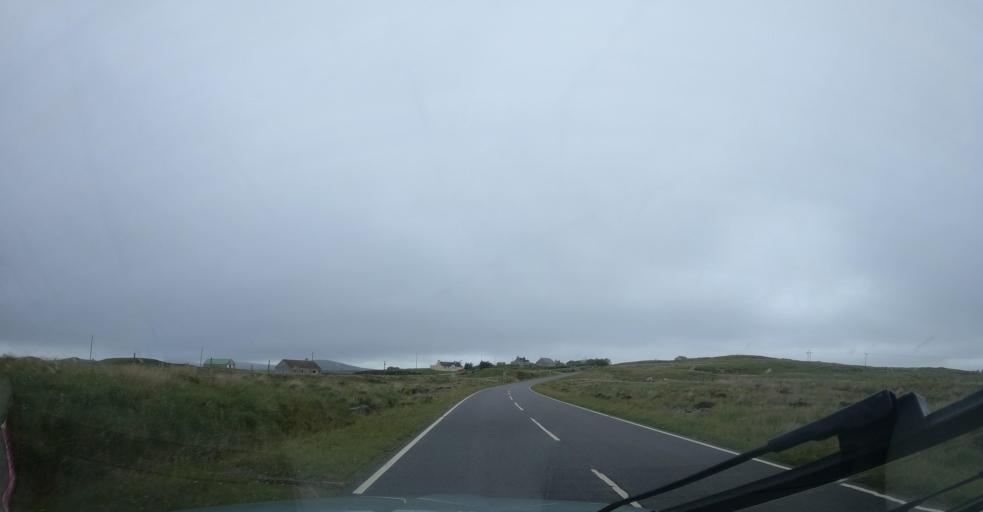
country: GB
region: Scotland
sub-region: Eilean Siar
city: Isle of North Uist
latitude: 57.6023
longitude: -7.1782
